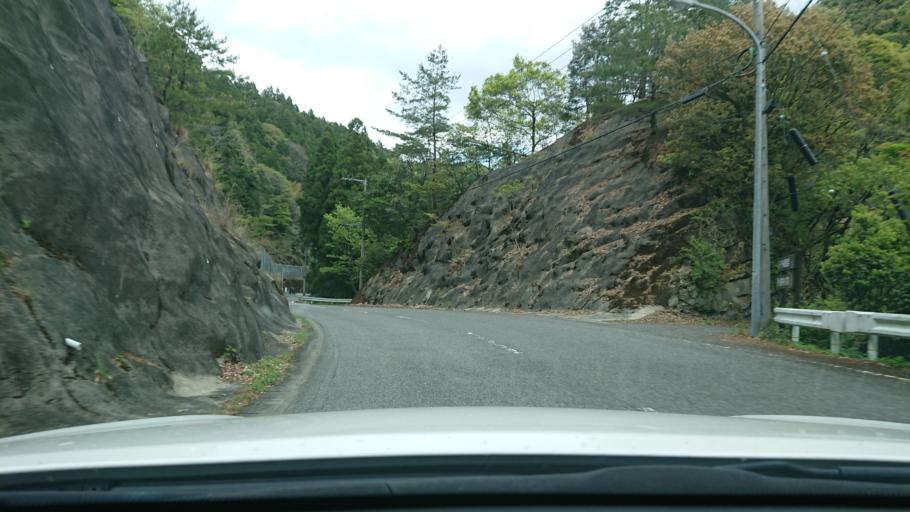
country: JP
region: Tokushima
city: Ishii
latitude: 33.9111
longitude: 134.4210
